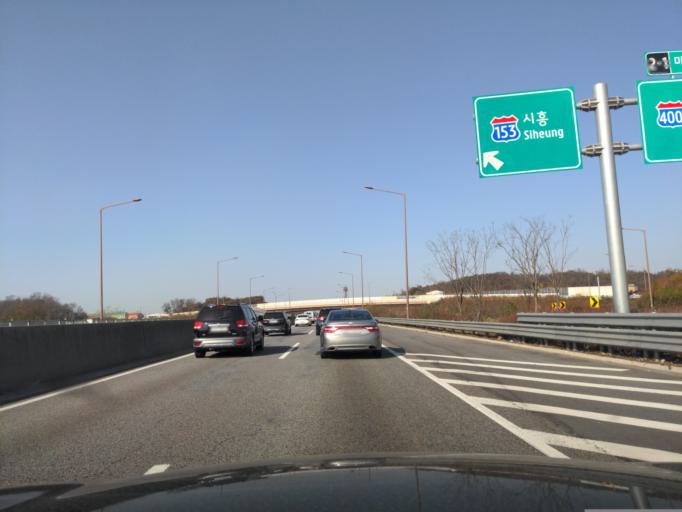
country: KR
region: Gyeonggi-do
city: Hwaseong-si
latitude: 37.1850
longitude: 126.7777
